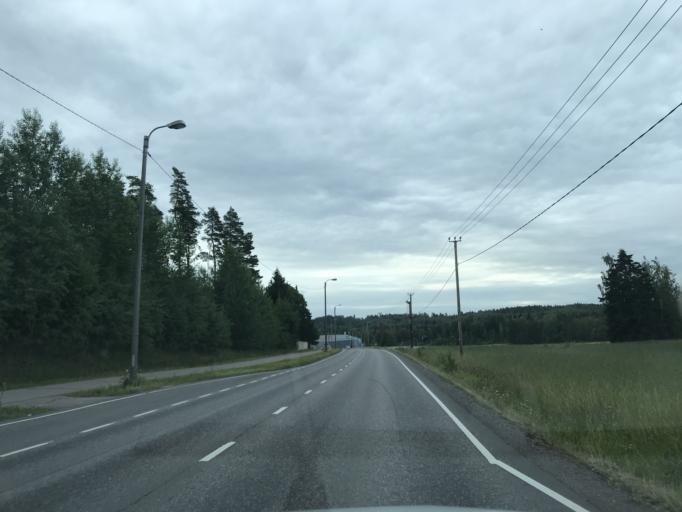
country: FI
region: Uusimaa
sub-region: Helsinki
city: Nurmijaervi
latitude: 60.3820
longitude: 24.7314
